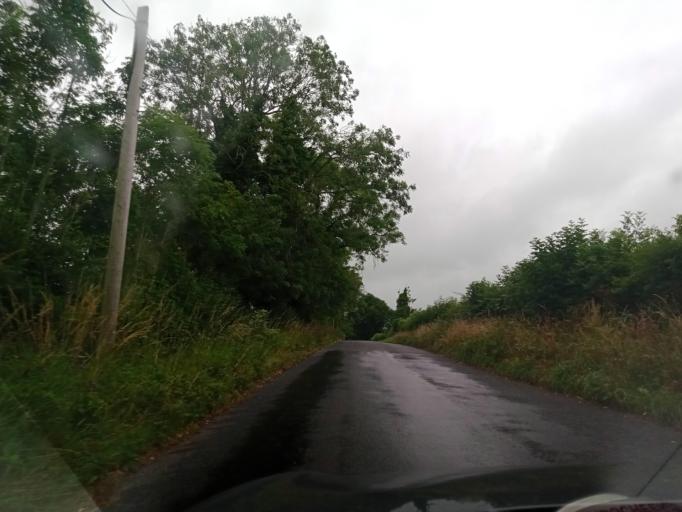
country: IE
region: Leinster
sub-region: Laois
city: Abbeyleix
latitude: 52.9171
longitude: -7.2885
